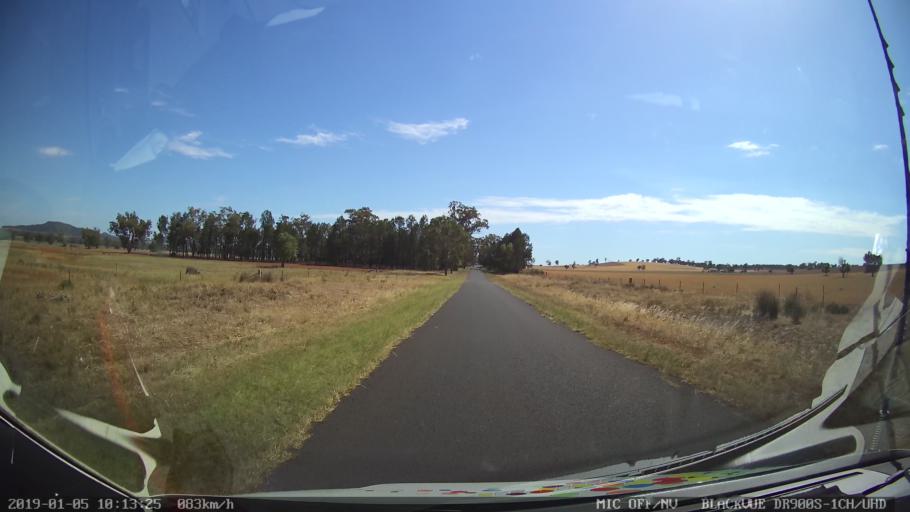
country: AU
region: New South Wales
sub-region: Gilgandra
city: Gilgandra
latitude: -31.6025
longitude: 148.9247
